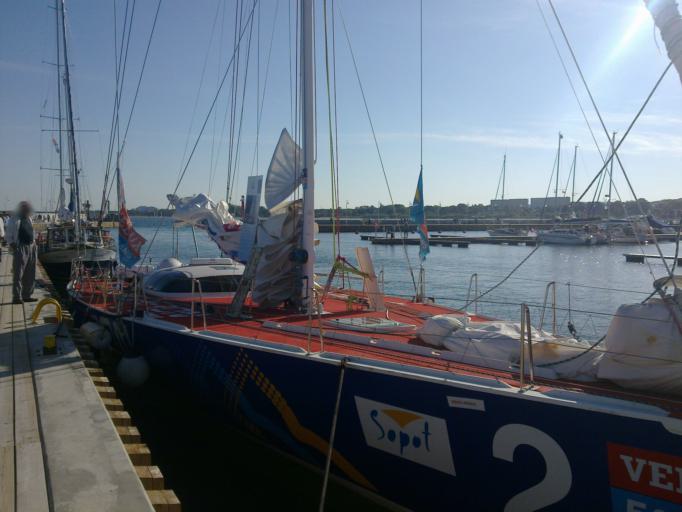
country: PL
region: Pomeranian Voivodeship
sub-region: Sopot
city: Sopot
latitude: 54.4482
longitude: 18.5783
